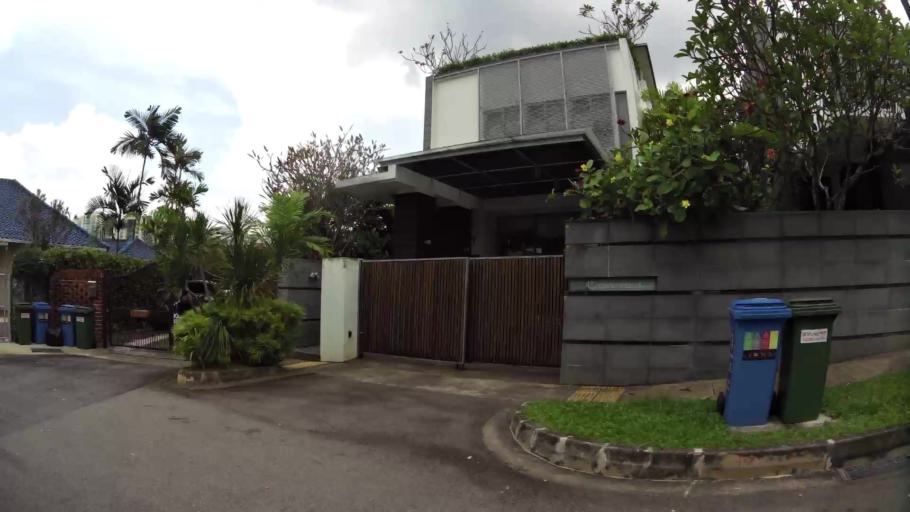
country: SG
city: Singapore
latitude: 1.3476
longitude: 103.8620
